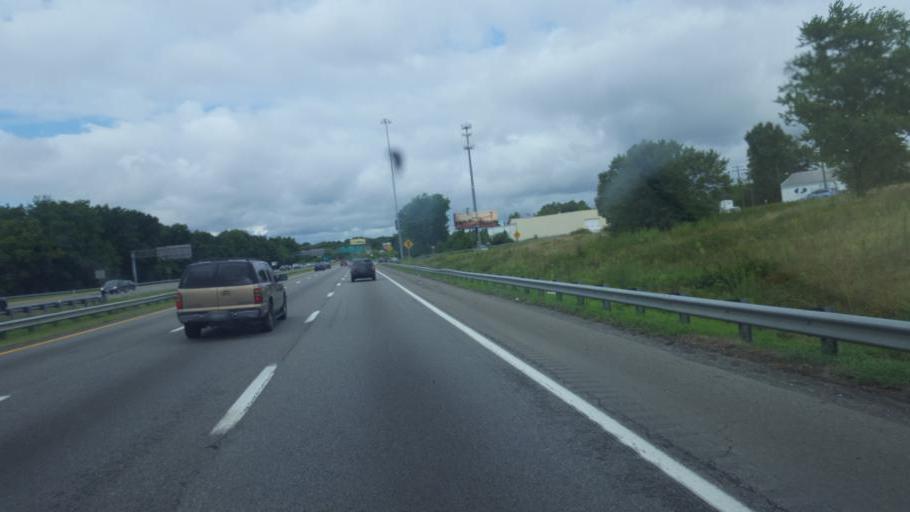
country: US
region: Virginia
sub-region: Henrico County
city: East Highland Park
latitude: 37.5563
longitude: -77.4103
